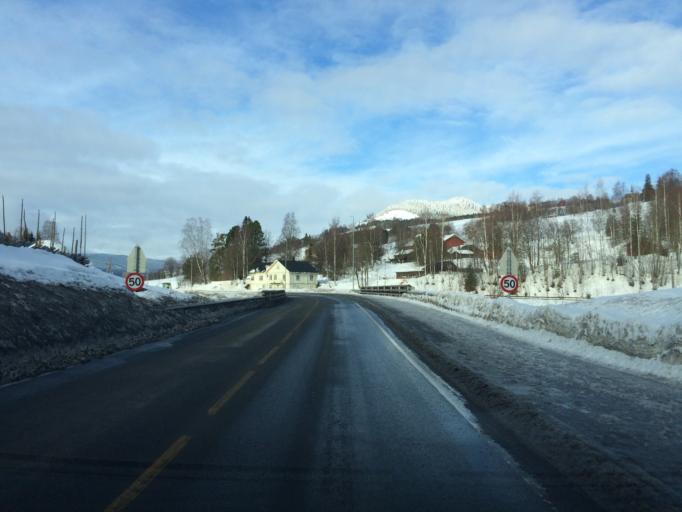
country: NO
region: Oppland
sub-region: Gausdal
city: Segalstad bru
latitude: 61.2185
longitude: 10.2759
